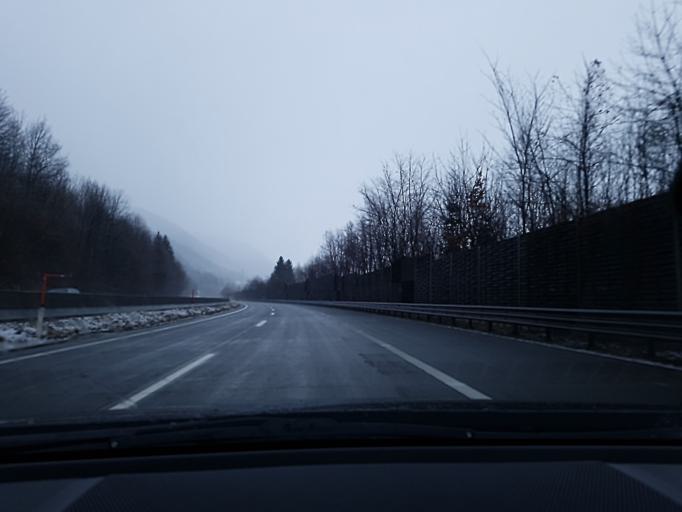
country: AT
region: Salzburg
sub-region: Politischer Bezirk Hallein
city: Kuchl
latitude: 47.6222
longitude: 13.1380
